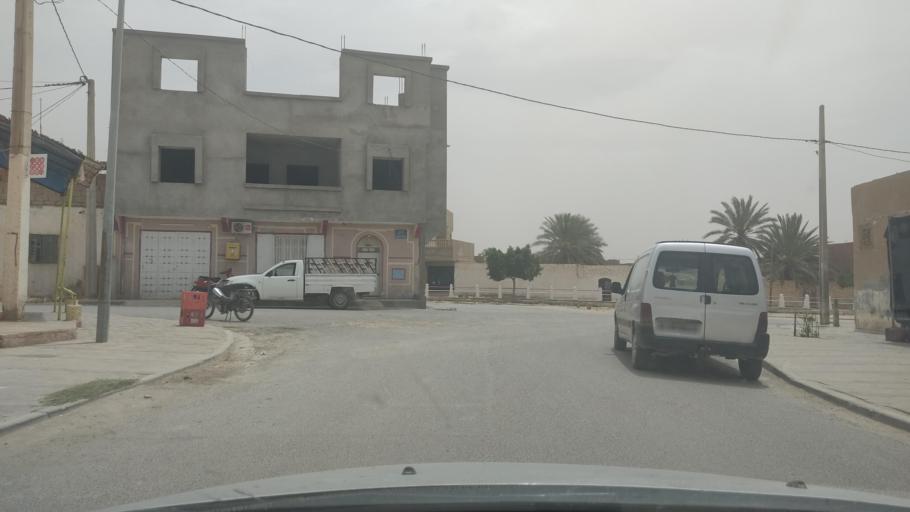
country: TN
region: Gafsa
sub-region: Gafsa Municipality
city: Gafsa
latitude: 34.3342
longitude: 8.9540
